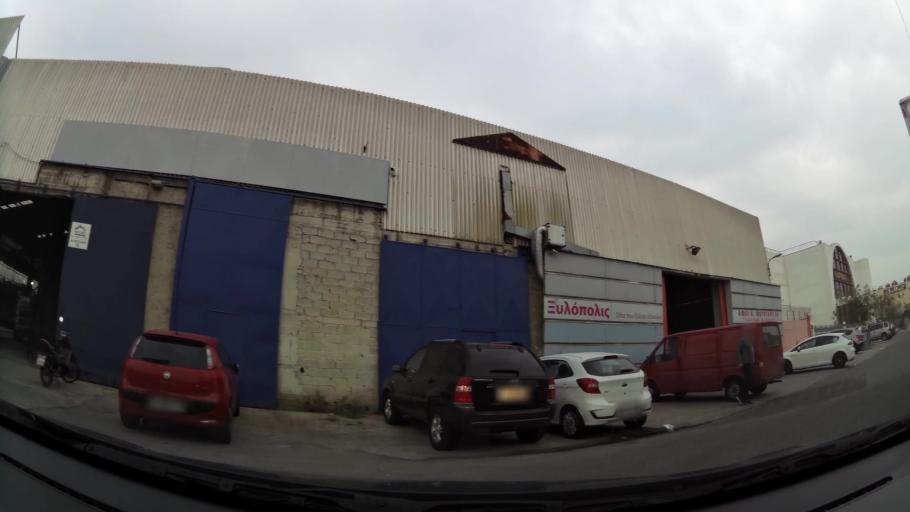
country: GR
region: Attica
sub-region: Nomos Piraios
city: Agios Ioannis Rentis
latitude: 37.9679
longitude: 23.6657
